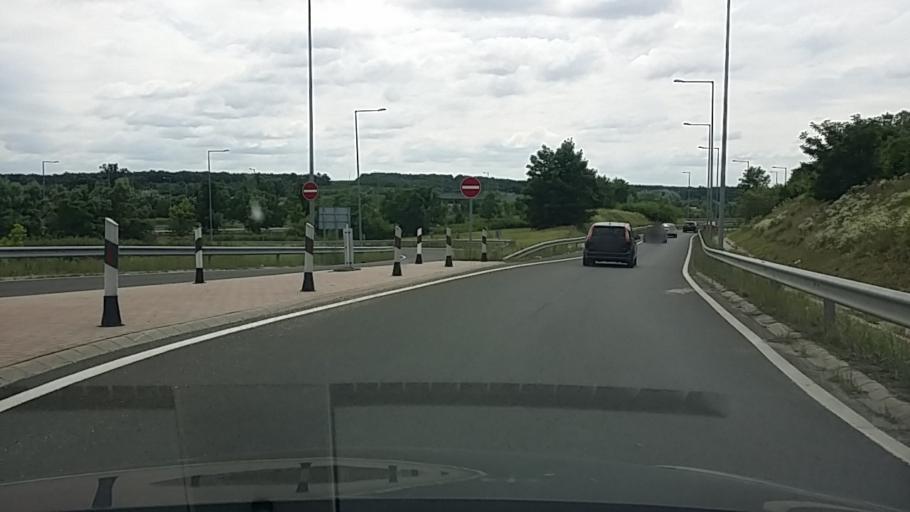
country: HU
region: Pest
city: Szada
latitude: 47.6155
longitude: 19.3251
